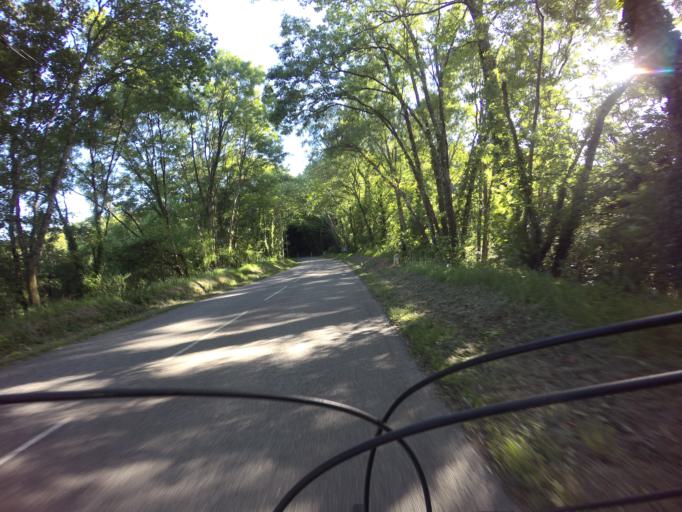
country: FR
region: Brittany
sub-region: Departement du Finistere
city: Quimper
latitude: 48.0187
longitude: -4.1351
